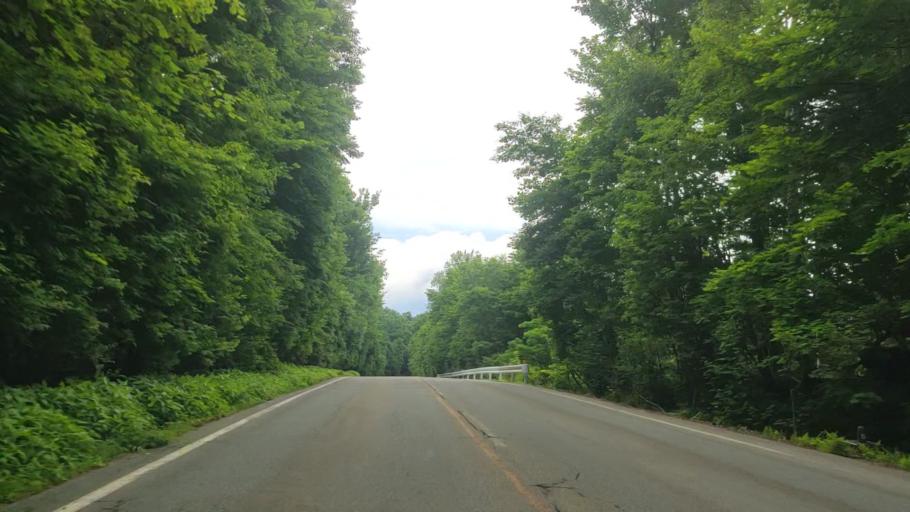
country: JP
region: Yamanashi
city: Fujikawaguchiko
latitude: 35.4151
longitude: 138.7384
